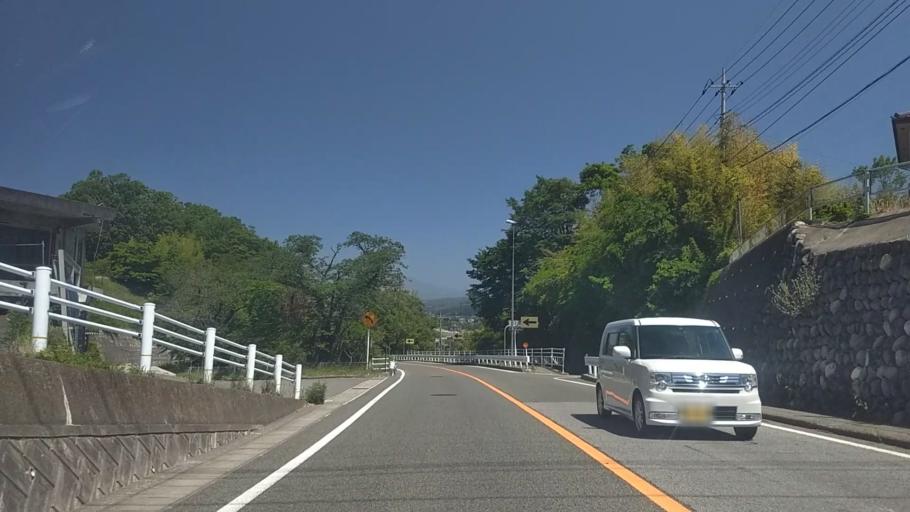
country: JP
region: Yamanashi
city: Nirasaki
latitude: 35.6836
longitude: 138.4629
